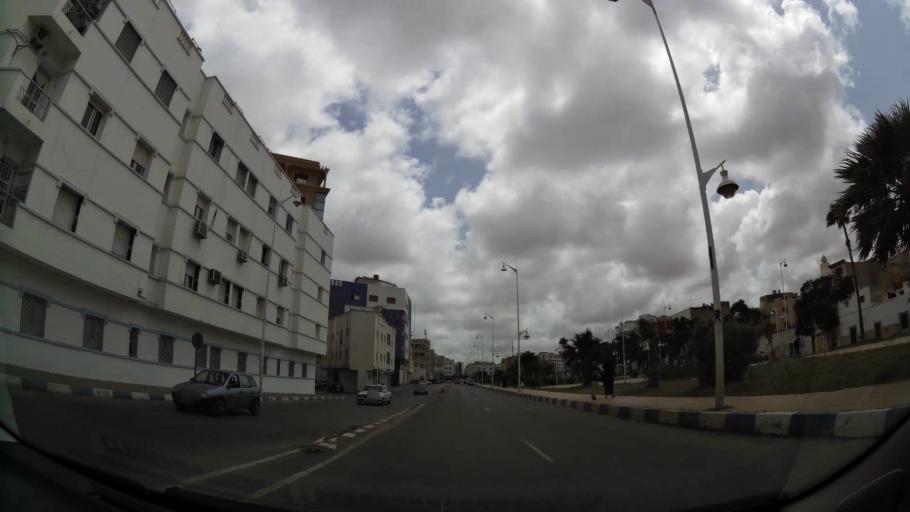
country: MA
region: Oriental
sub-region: Nador
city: Nador
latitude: 35.1820
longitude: -2.9279
